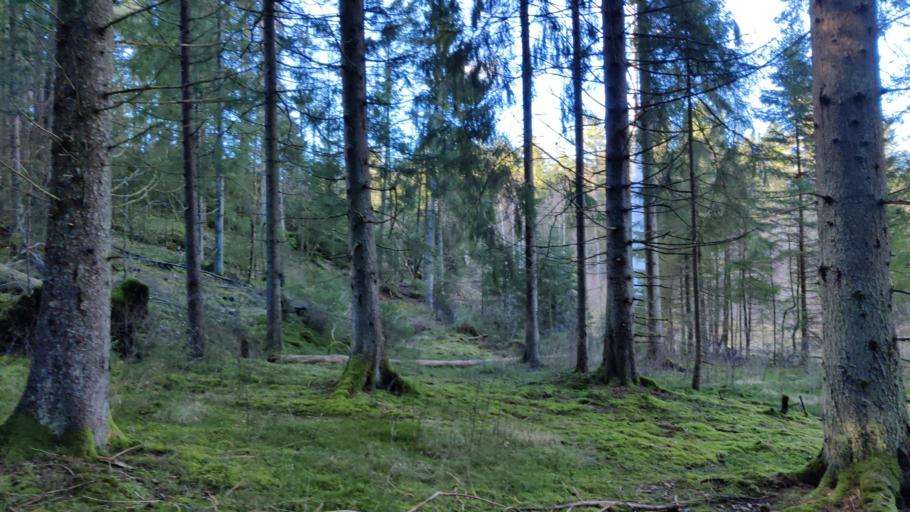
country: SE
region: Vaestra Goetaland
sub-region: Uddevalla Kommun
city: Uddevalla
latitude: 58.3489
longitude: 11.9681
